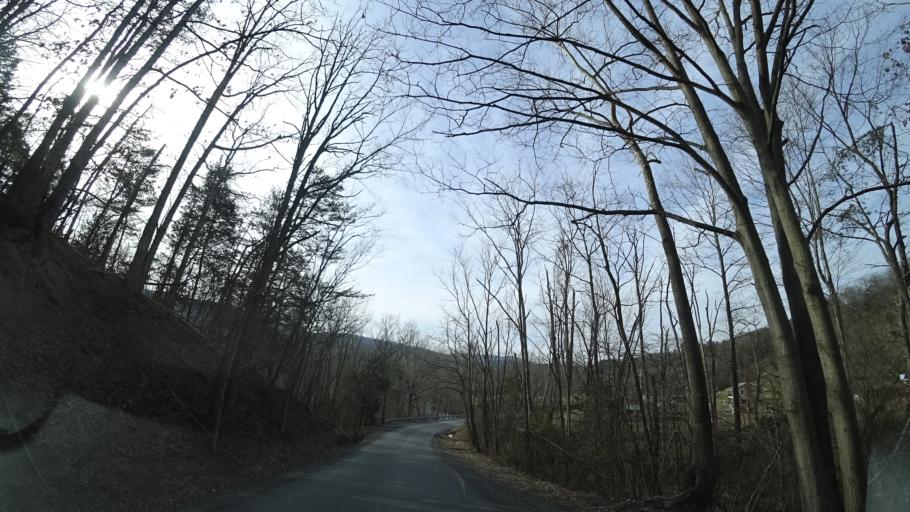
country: US
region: Virginia
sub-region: Shenandoah County
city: Woodstock
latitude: 39.0725
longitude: -78.6254
